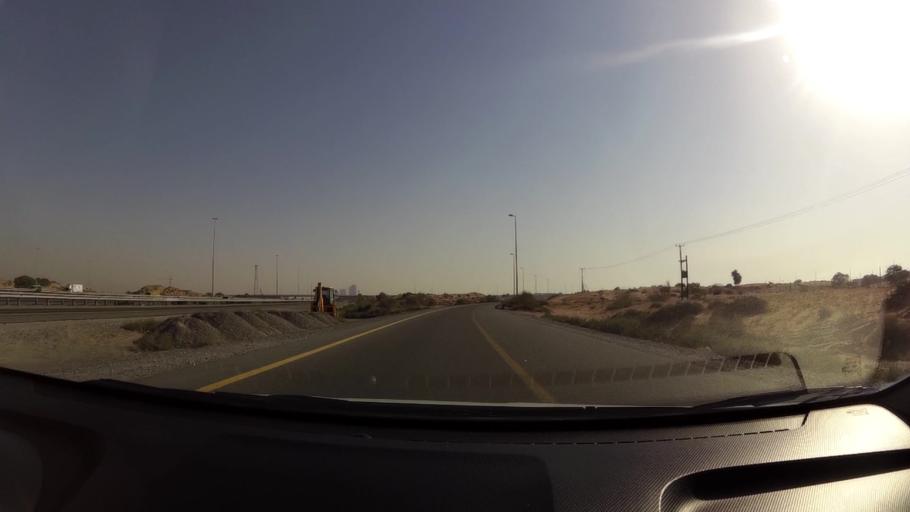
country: AE
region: Umm al Qaywayn
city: Umm al Qaywayn
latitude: 25.4323
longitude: 55.5957
